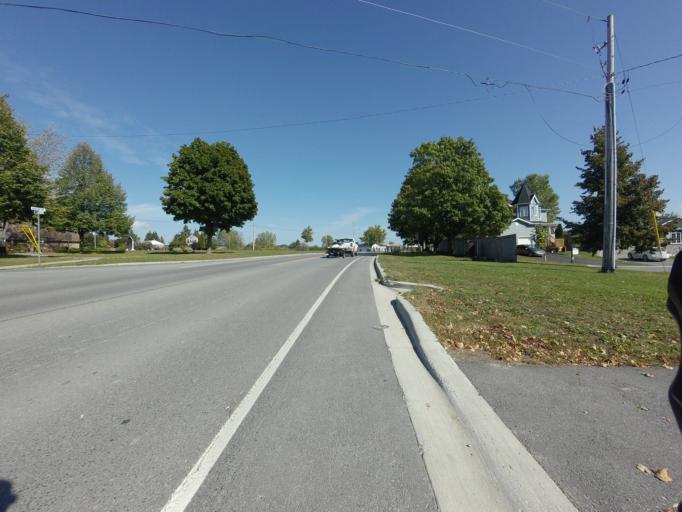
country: CA
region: Ontario
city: Skatepark
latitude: 44.1846
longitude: -76.7714
